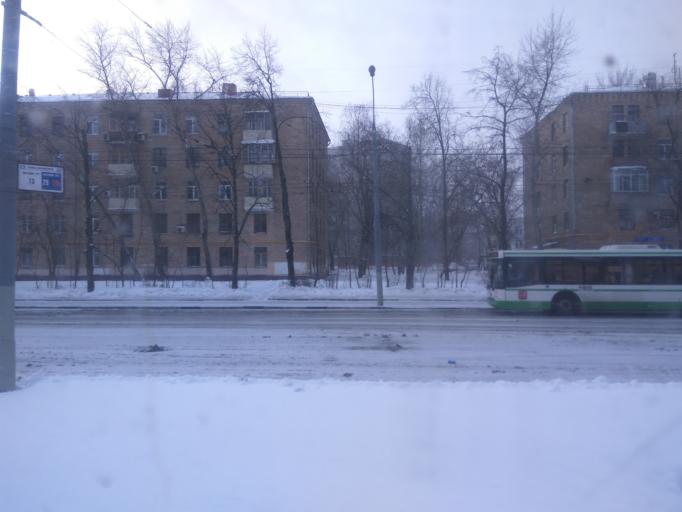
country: RU
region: Moscow
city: Ostankinskiy
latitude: 55.8207
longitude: 37.5909
